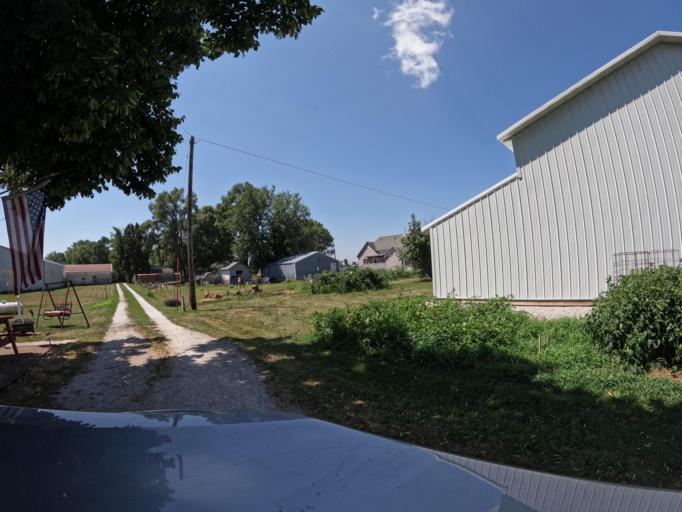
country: US
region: Iowa
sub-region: Keokuk County
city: Sigourney
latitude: 41.2639
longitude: -92.2496
